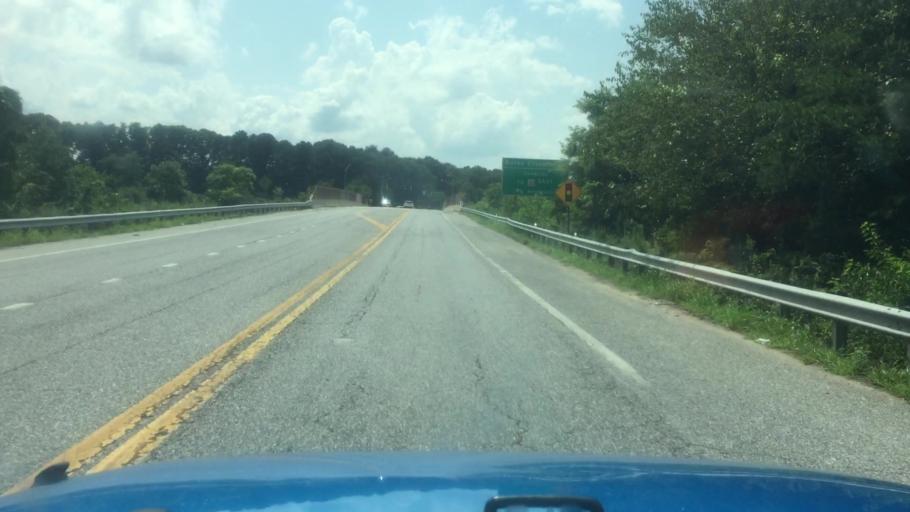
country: US
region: Maryland
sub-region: Anne Arundel County
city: Gambrills
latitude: 39.0811
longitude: -76.6765
